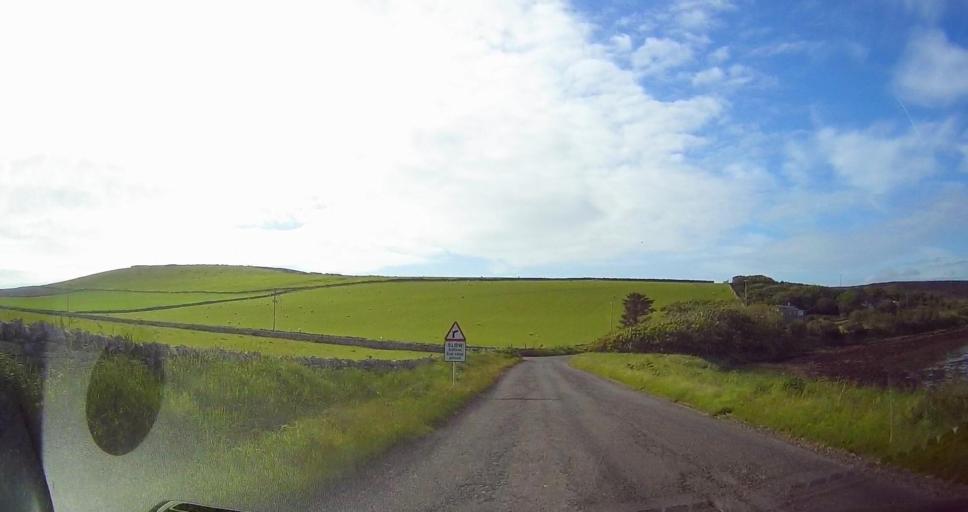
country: GB
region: Scotland
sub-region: Orkney Islands
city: Stromness
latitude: 58.7863
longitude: -3.2588
